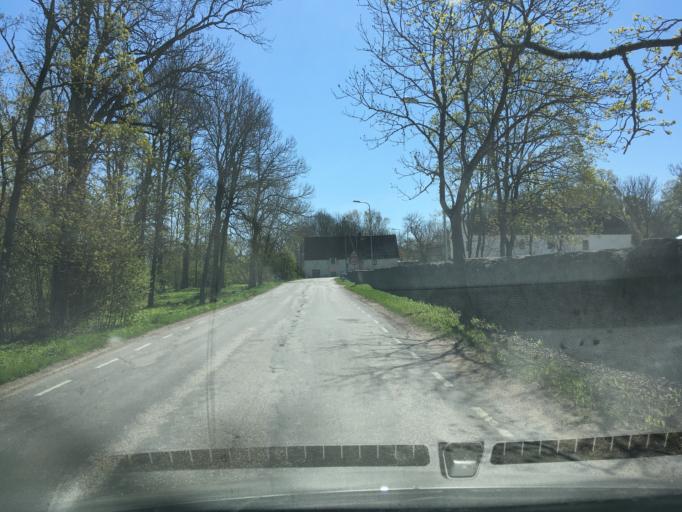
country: EE
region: Harju
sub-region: Raasiku vald
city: Arukula
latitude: 59.3595
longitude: 25.0827
